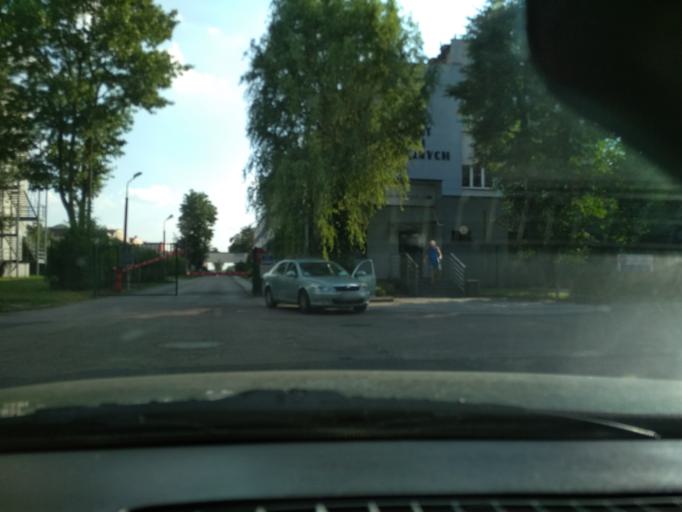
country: PL
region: Silesian Voivodeship
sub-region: Gliwice
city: Gliwice
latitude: 50.2968
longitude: 18.6362
